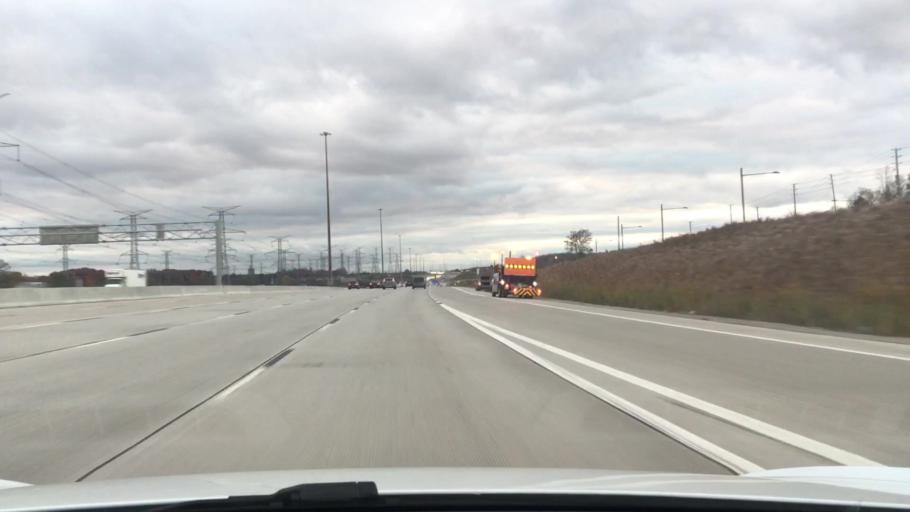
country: CA
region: Ontario
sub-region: York
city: Richmond Hill
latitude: 43.8327
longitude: -79.4339
